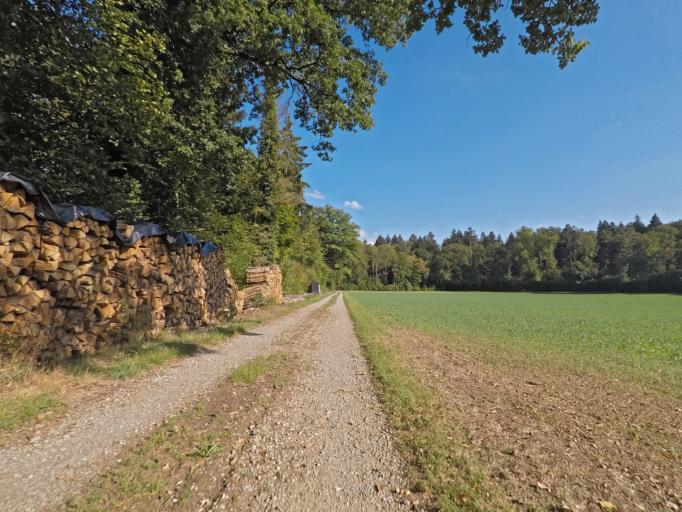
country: CH
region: Thurgau
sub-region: Frauenfeld District
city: Diessenhofen
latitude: 47.6573
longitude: 8.7395
